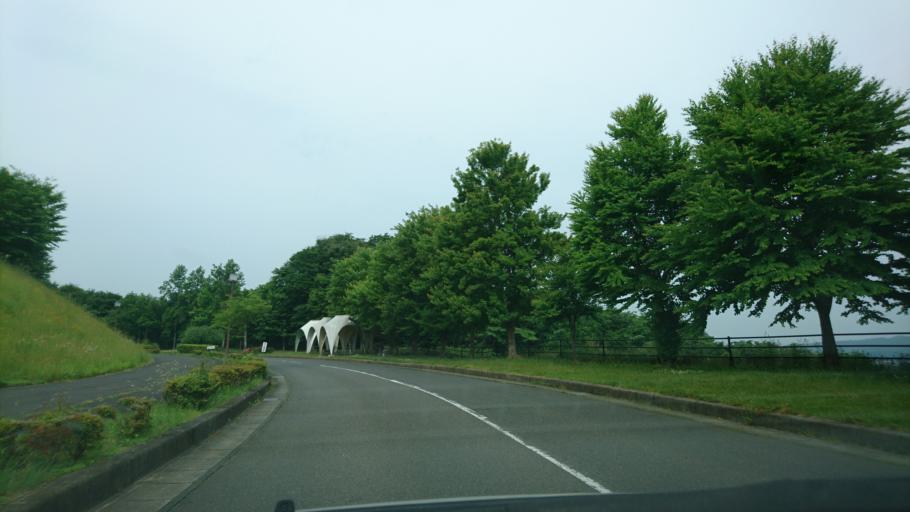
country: JP
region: Iwate
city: Ichinoseki
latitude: 38.9201
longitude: 141.1239
